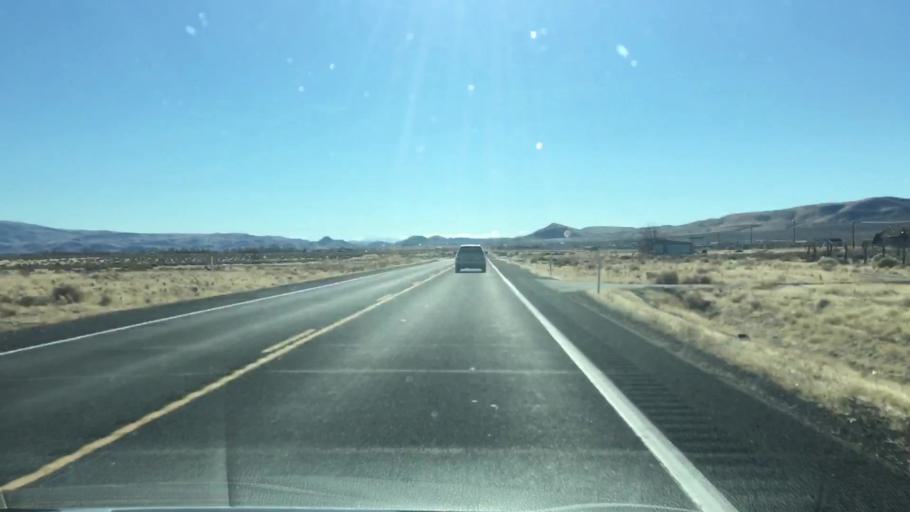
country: US
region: Nevada
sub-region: Lyon County
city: Silver Springs
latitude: 39.3841
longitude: -119.2318
